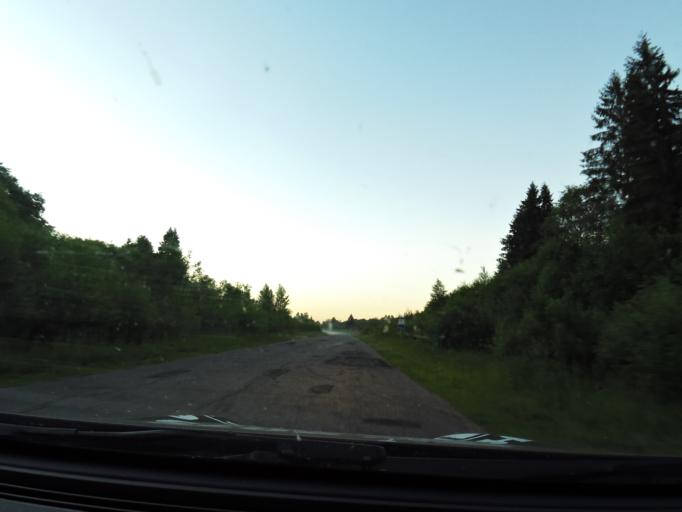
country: RU
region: Kostroma
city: Buy
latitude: 58.3878
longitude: 41.2214
